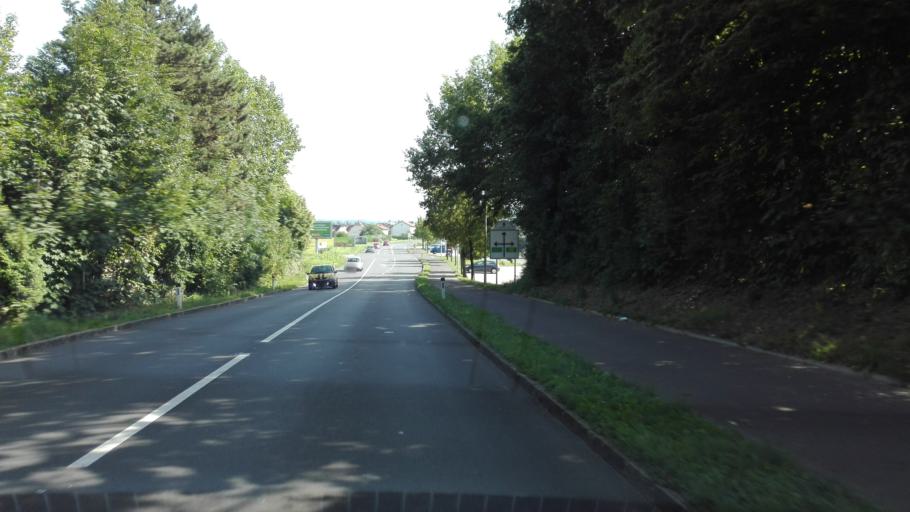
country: AT
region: Upper Austria
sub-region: Politischer Bezirk Linz-Land
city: Leonding
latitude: 48.2566
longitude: 14.2602
